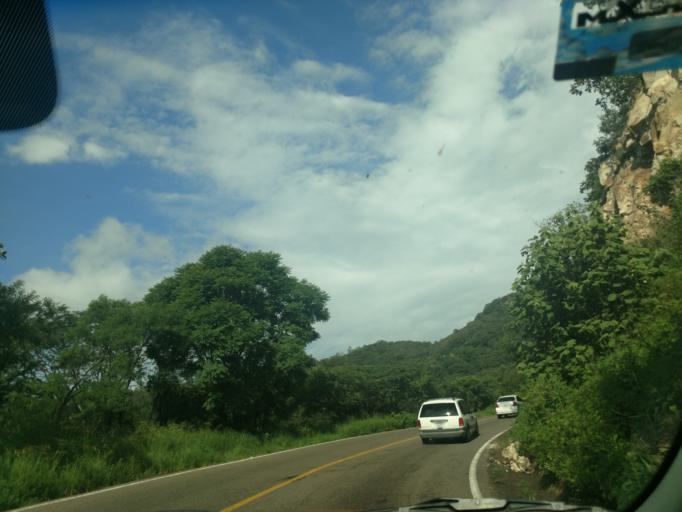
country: MX
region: Jalisco
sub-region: Atengo
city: Soyatlan del Oro
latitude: 20.4857
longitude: -104.3629
